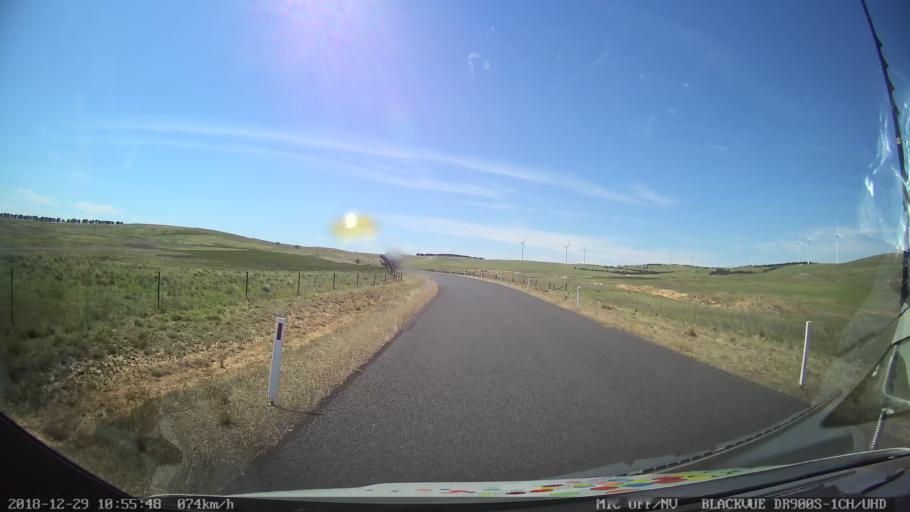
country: AU
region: New South Wales
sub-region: Palerang
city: Bungendore
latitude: -35.1281
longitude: 149.5336
